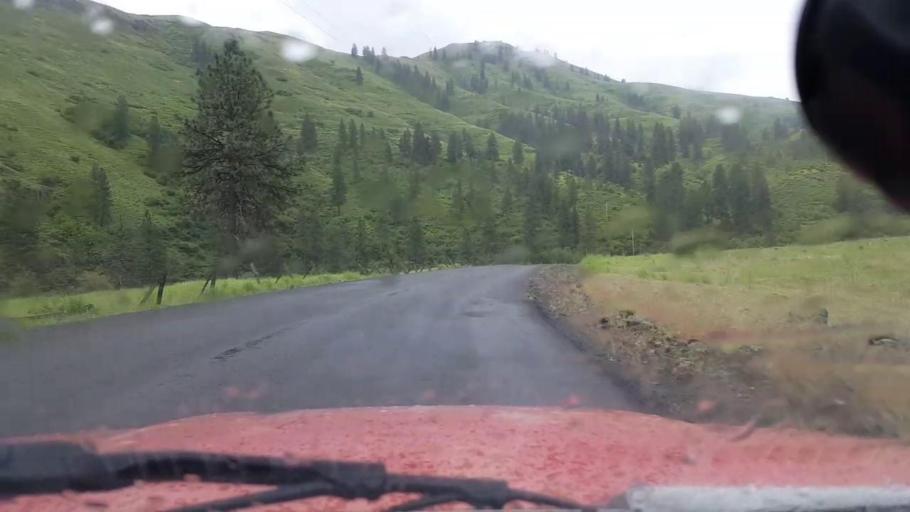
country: US
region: Washington
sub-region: Asotin County
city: Asotin
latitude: 46.0280
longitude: -117.3244
